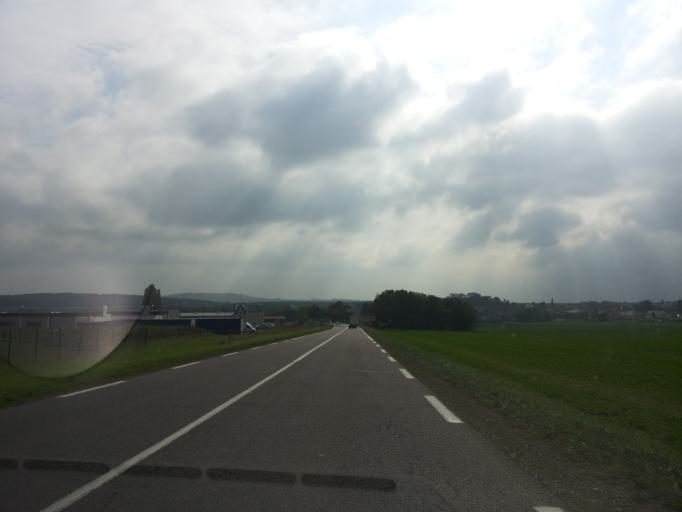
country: FR
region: Lorraine
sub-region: Departement de la Moselle
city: Solgne
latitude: 48.9741
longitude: 6.2938
